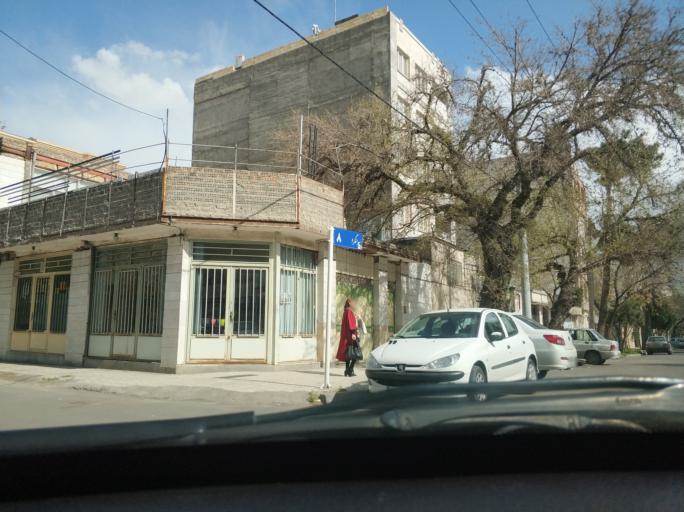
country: IR
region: Razavi Khorasan
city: Mashhad
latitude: 36.2715
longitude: 59.5912
